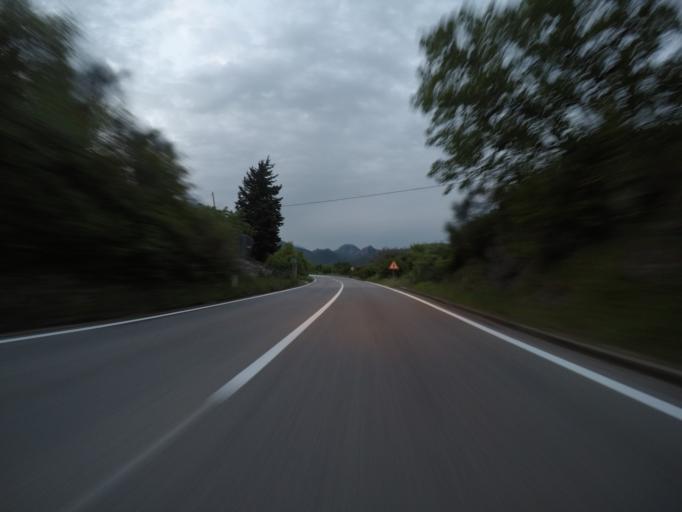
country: ME
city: Petrovac na Moru
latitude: 42.2025
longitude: 18.9598
